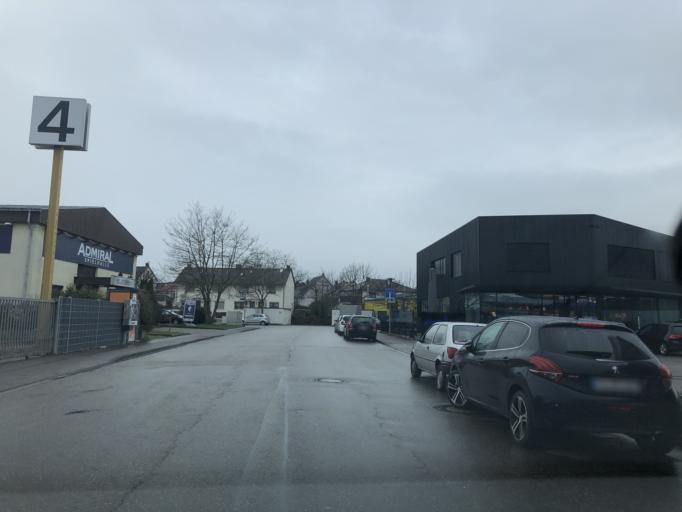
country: DE
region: Baden-Wuerttemberg
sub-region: Karlsruhe Region
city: Rastatt
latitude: 48.8599
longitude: 8.2295
